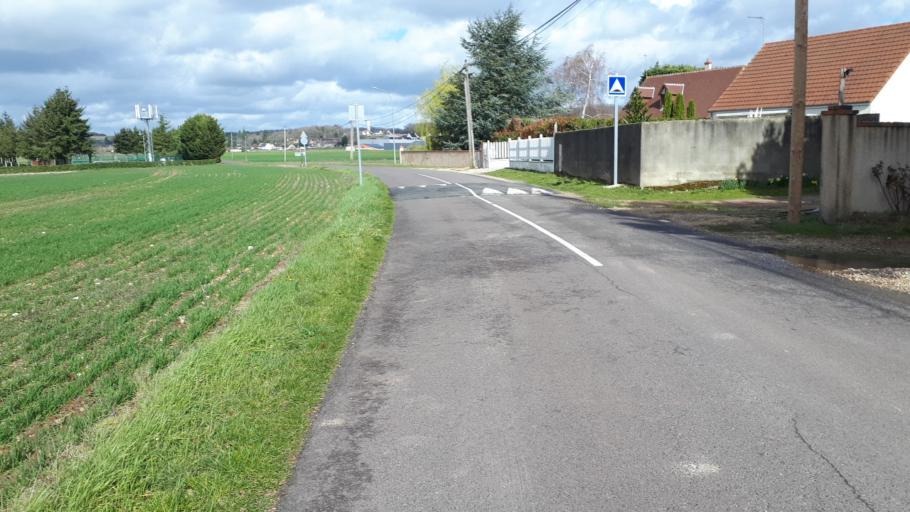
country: FR
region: Centre
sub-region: Departement du Loir-et-Cher
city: Villiers-sur-Loir
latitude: 47.7937
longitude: 1.0015
